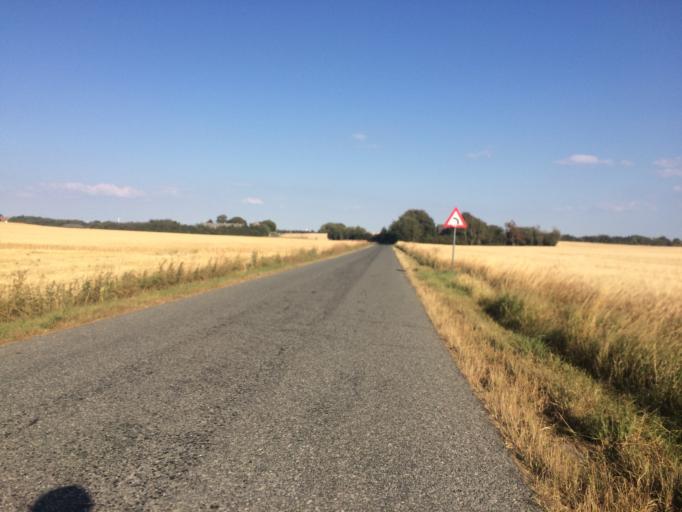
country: DK
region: Central Jutland
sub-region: Holstebro Kommune
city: Vinderup
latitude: 56.5876
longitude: 8.7684
